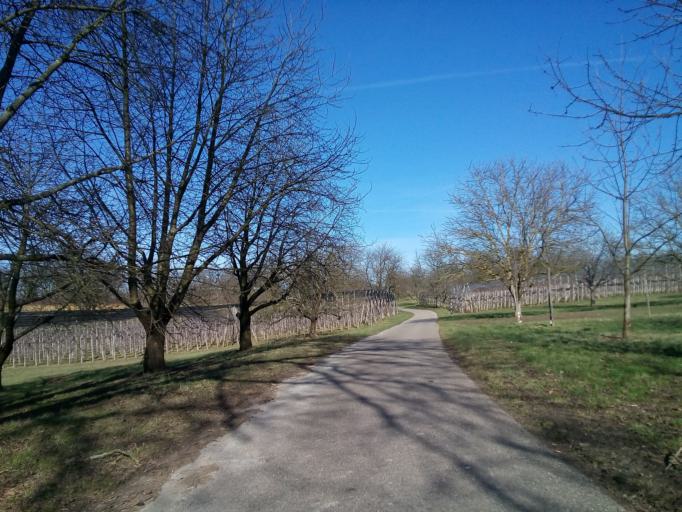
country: DE
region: Baden-Wuerttemberg
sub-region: Freiburg Region
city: Achern
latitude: 48.6075
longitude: 8.0595
